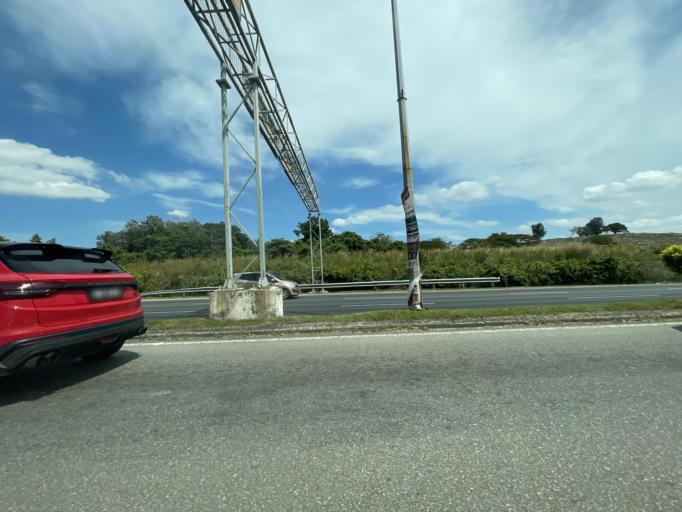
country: MY
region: Melaka
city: Batu Berendam
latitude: 2.2429
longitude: 102.2233
